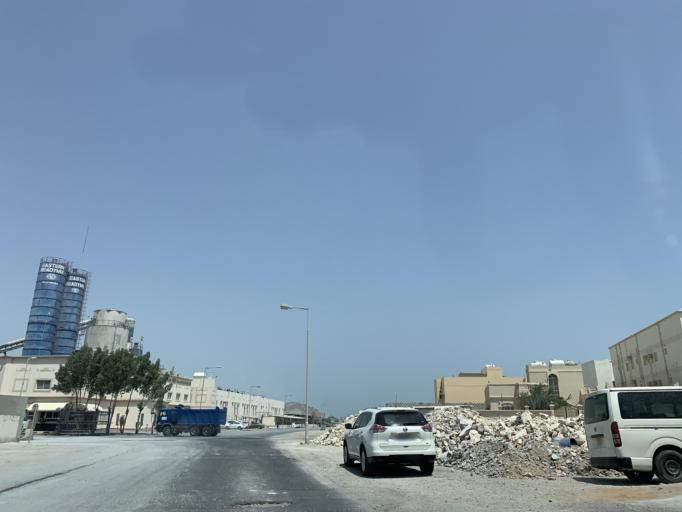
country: BH
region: Northern
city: Sitrah
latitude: 26.1462
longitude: 50.5991
